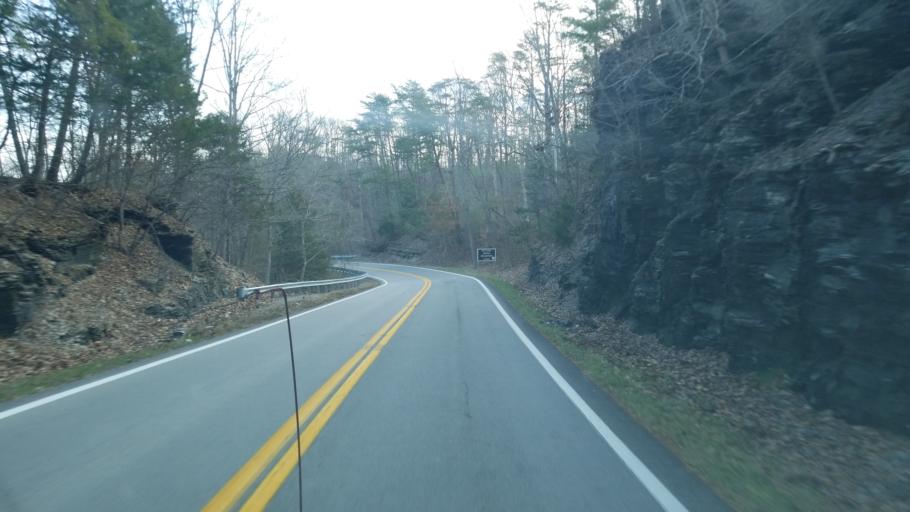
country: US
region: Kentucky
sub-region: Russell County
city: Jamestown
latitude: 36.8586
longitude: -85.1535
